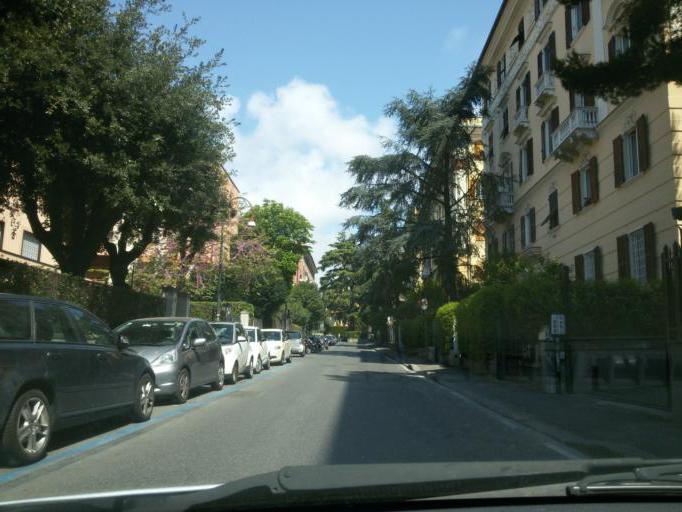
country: IT
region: Liguria
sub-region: Provincia di Genova
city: San Teodoro
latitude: 44.3977
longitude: 8.9590
